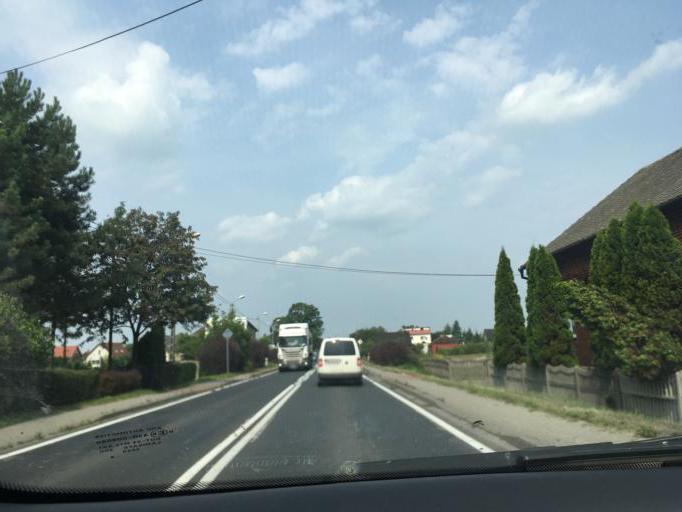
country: PL
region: Lesser Poland Voivodeship
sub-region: Powiat oswiecimski
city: Babice
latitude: 50.0491
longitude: 19.2051
